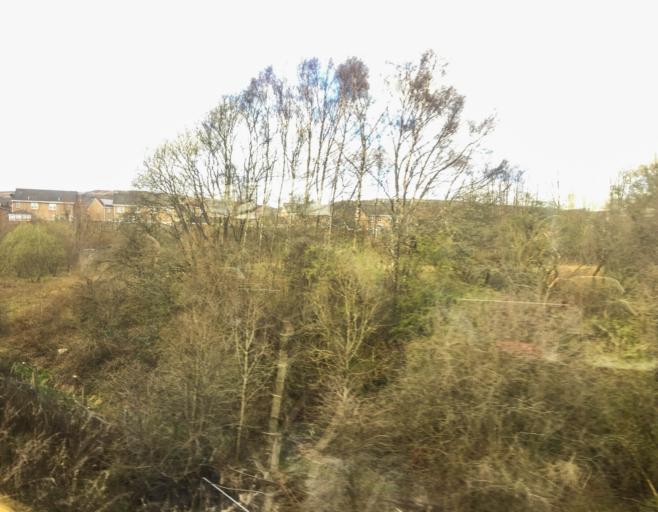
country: GB
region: Scotland
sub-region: West Dunbartonshire
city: Old Kilpatrick
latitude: 55.9195
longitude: -4.4443
